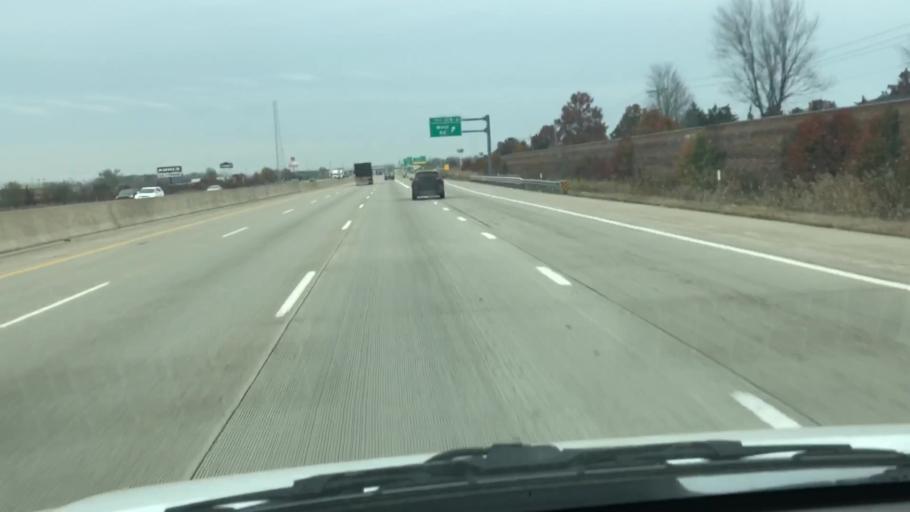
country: US
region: Michigan
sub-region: Wayne County
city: Woodhaven
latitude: 42.1460
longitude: -83.2421
